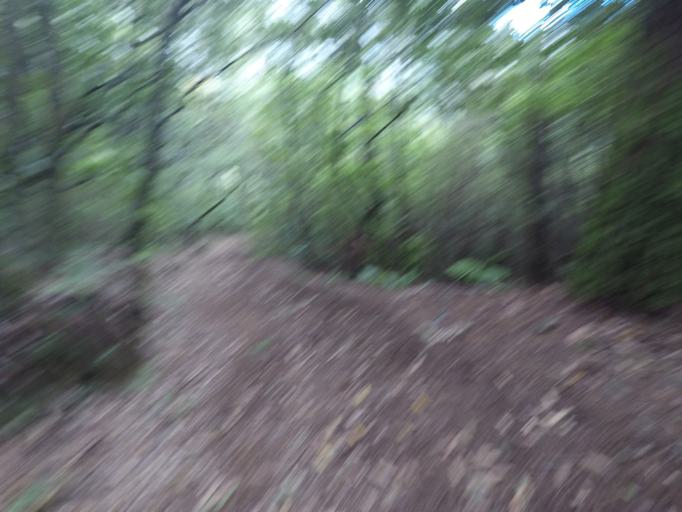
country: PT
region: Madeira
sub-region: Camara de Lobos
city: Curral das Freiras
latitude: 32.7748
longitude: -16.9801
